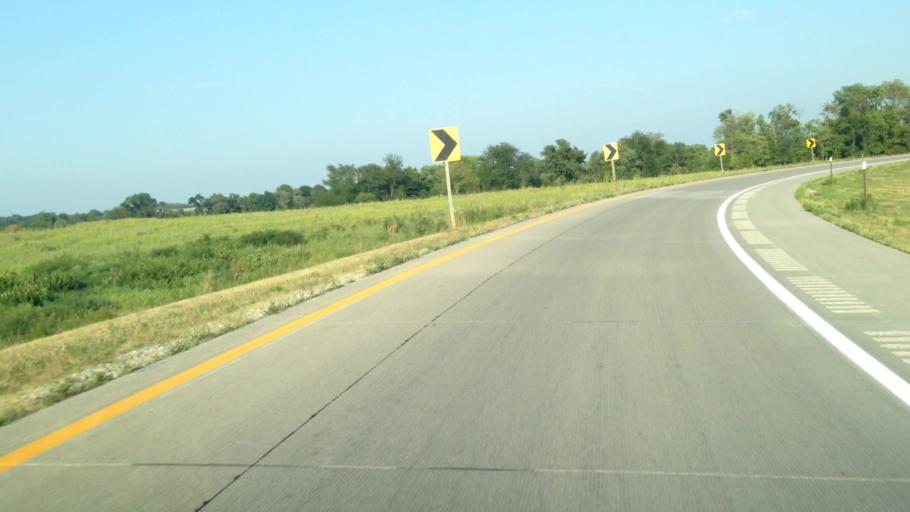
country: US
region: Kansas
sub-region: Franklin County
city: Ottawa
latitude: 38.6390
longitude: -95.2183
